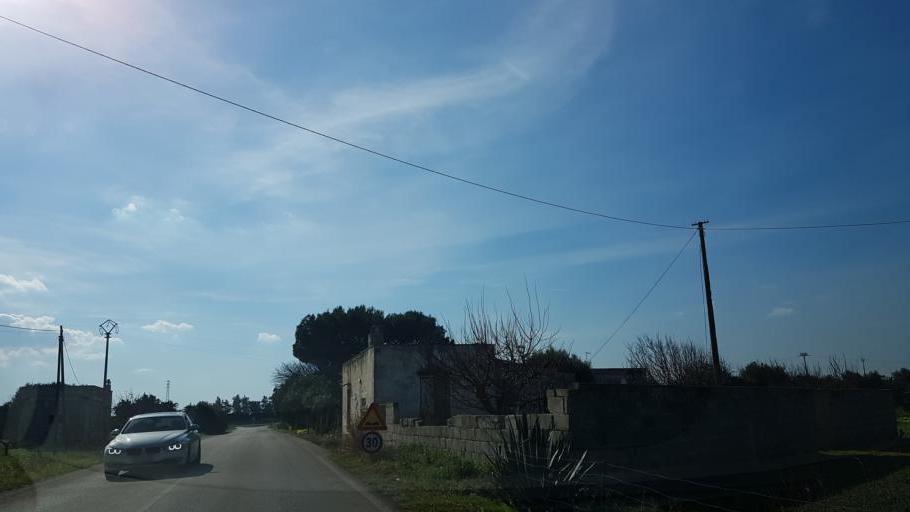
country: IT
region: Apulia
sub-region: Provincia di Brindisi
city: San Vito dei Normanni
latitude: 40.6918
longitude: 17.8247
